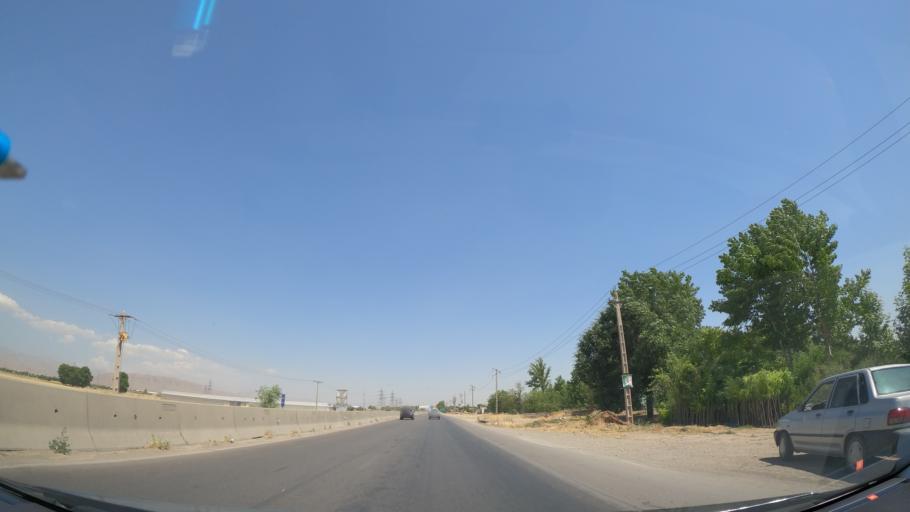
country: IR
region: Alborz
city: Hashtgerd
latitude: 35.9263
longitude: 50.7361
